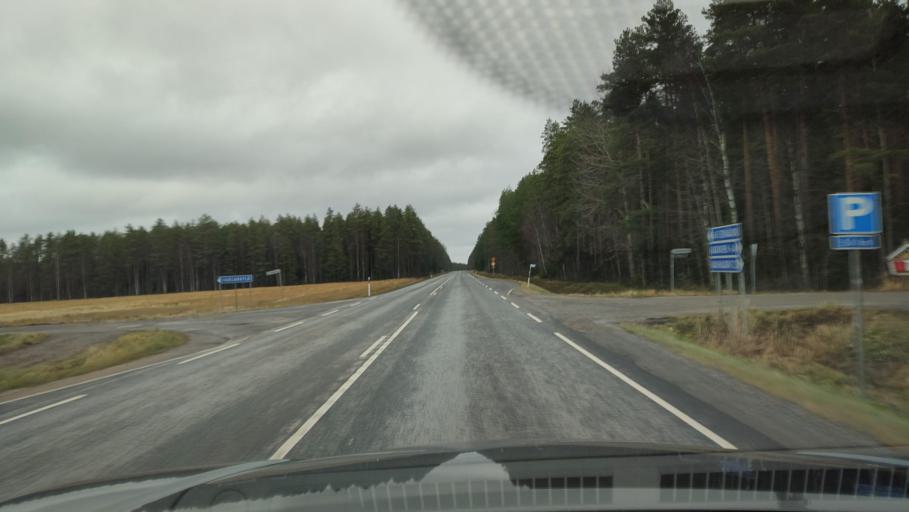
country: FI
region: Southern Ostrobothnia
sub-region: Suupohja
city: Kauhajoki
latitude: 62.5062
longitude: 22.3062
